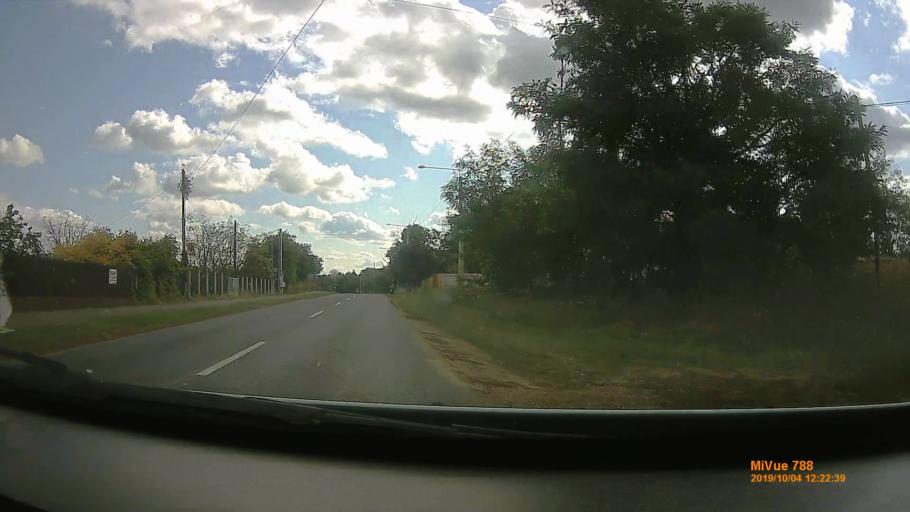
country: HU
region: Szabolcs-Szatmar-Bereg
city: Kotaj
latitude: 48.0114
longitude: 21.6918
